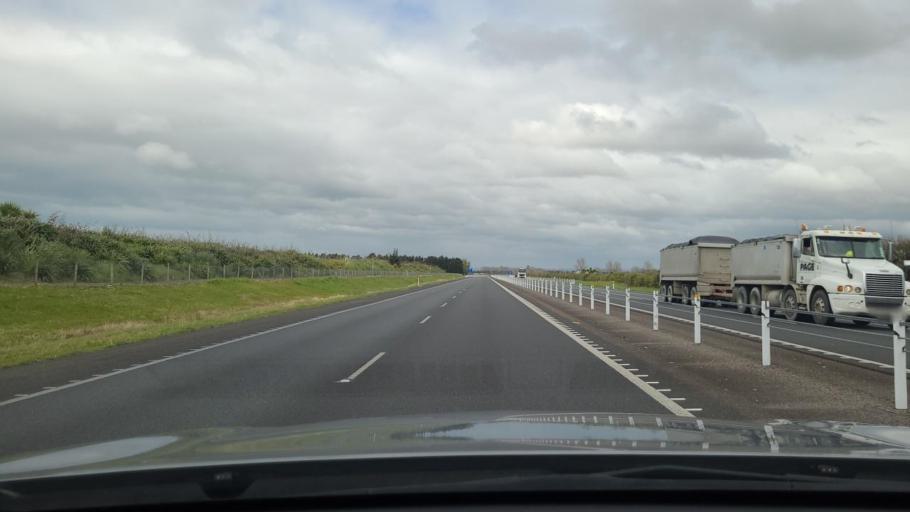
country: NZ
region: Bay of Plenty
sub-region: Western Bay of Plenty District
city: Maketu
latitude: -37.7570
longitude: 176.3643
